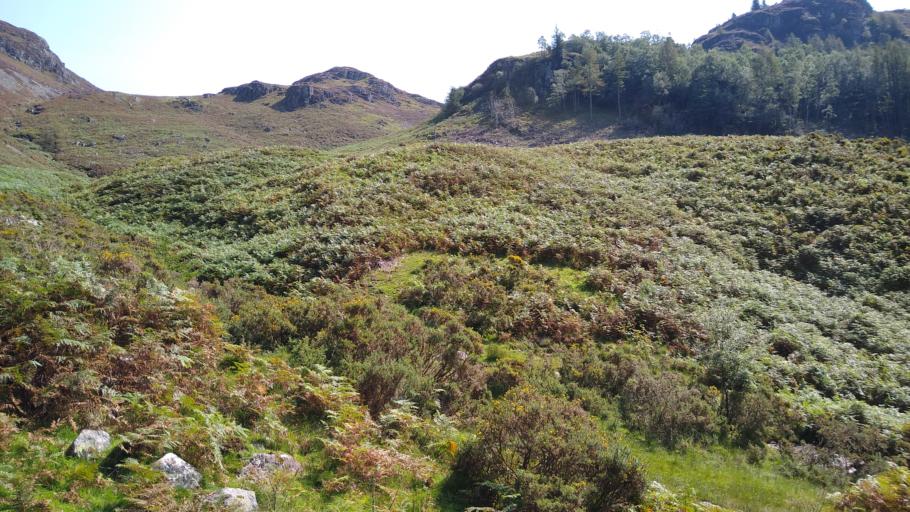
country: GB
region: England
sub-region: Cumbria
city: Frizington
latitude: 54.5319
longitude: -3.3759
